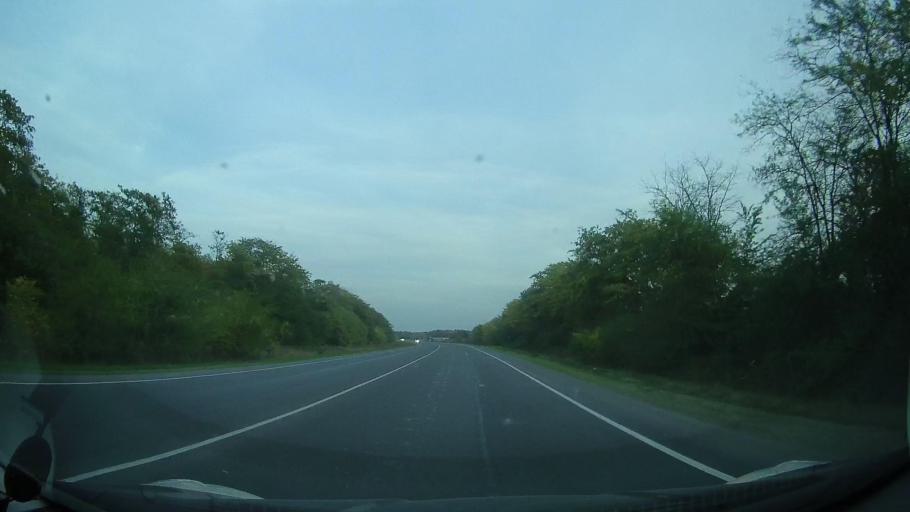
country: RU
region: Rostov
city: Kirovskaya
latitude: 46.9977
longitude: 39.9968
